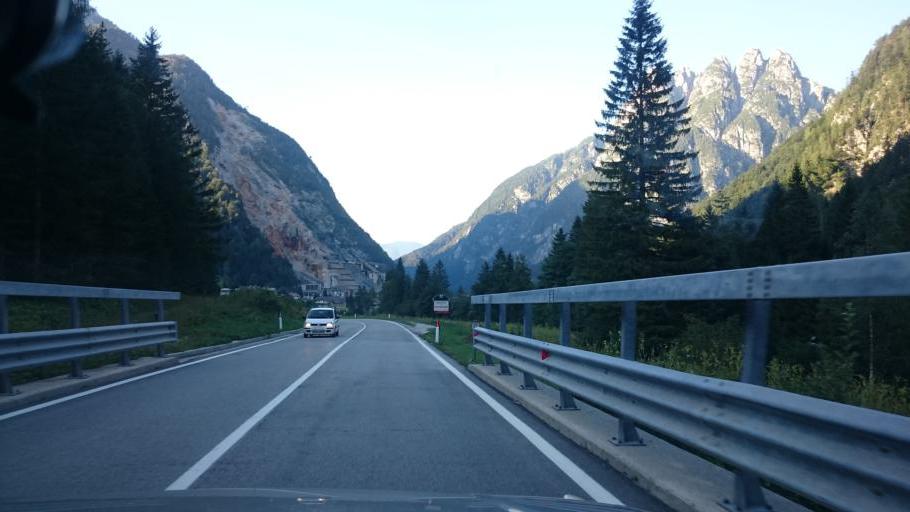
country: IT
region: Friuli Venezia Giulia
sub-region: Provincia di Udine
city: Tarvisio
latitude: 46.4340
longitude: 13.5682
